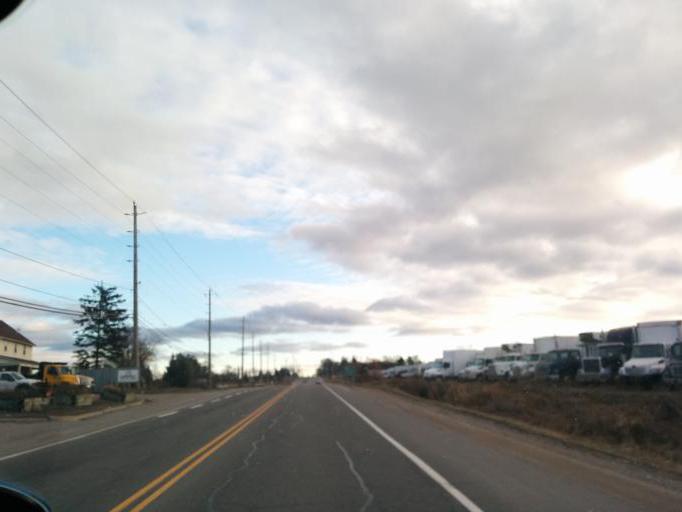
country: CA
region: Ontario
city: Bradford West Gwillimbury
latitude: 43.9953
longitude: -79.6748
